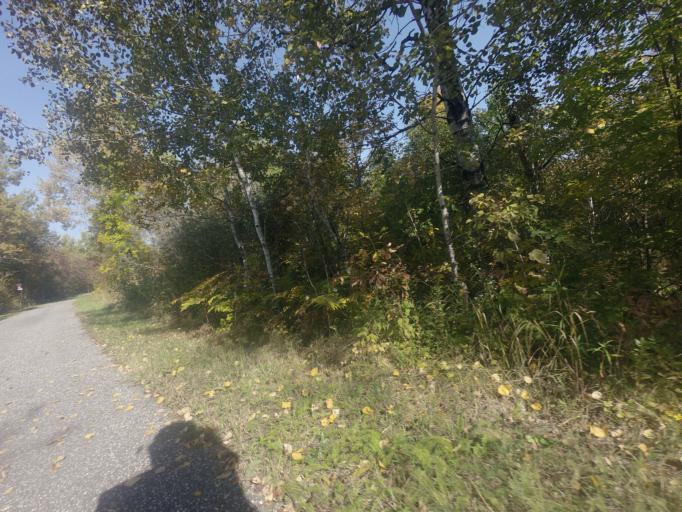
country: CA
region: Quebec
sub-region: Laurentides
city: Mont-Laurier
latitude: 46.5200
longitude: -75.4442
